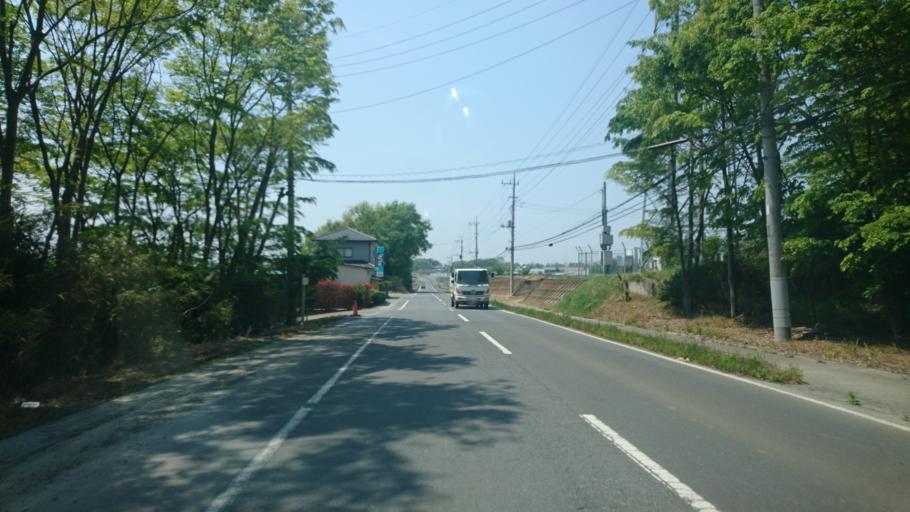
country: JP
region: Ibaraki
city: Shimodate
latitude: 36.2553
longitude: 139.9679
